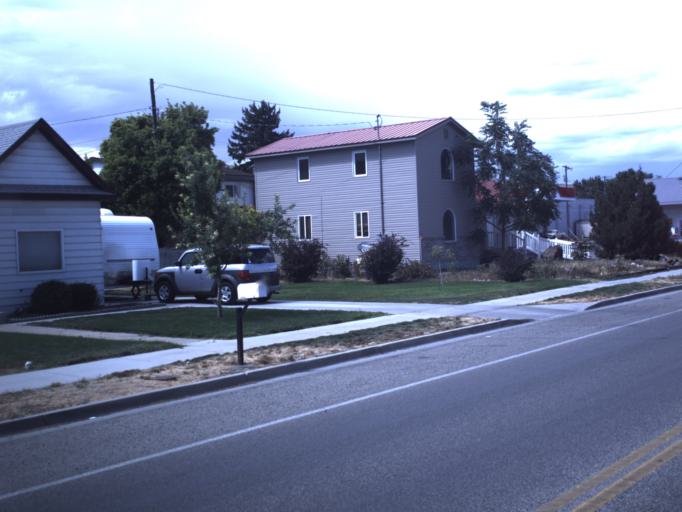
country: US
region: Utah
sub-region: Box Elder County
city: Garland
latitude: 41.7395
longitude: -112.1626
